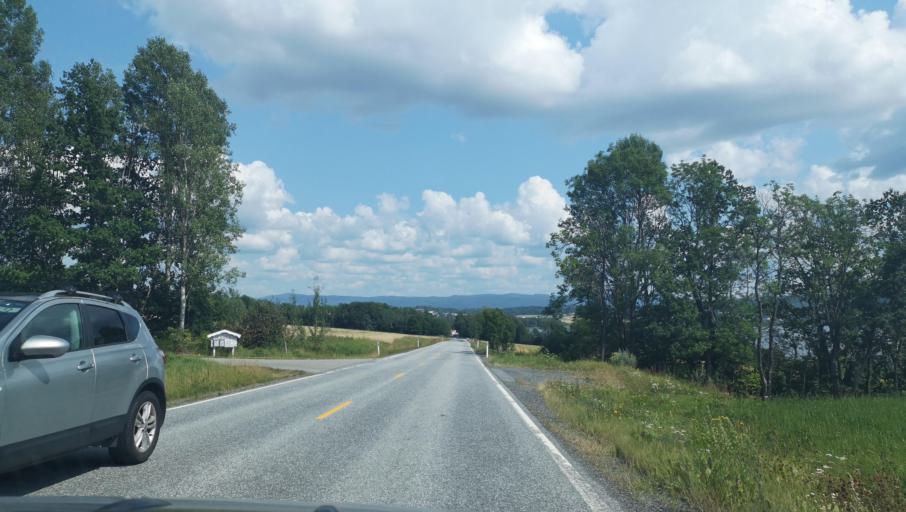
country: NO
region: Buskerud
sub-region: Ovre Eiker
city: Hokksund
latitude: 59.7058
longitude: 9.8101
